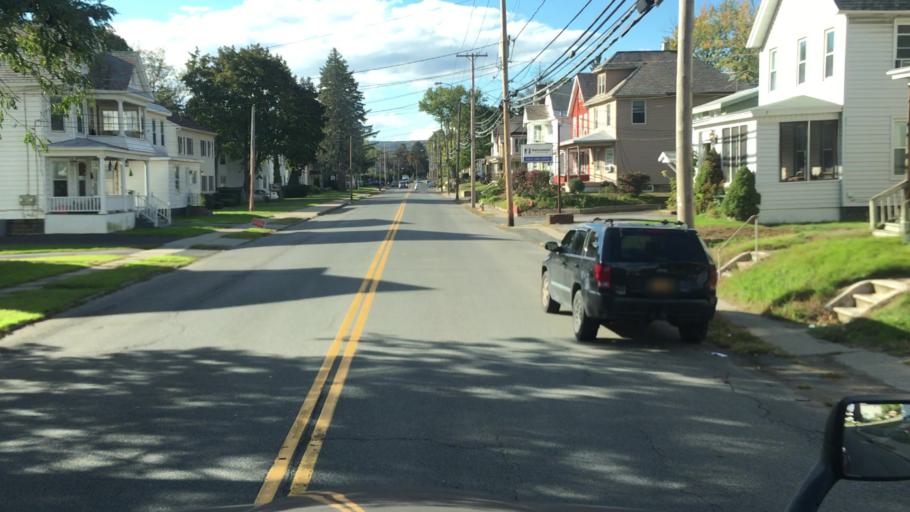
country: US
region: New York
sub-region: Schenectady County
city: Scotia
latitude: 42.8281
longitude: -73.9696
